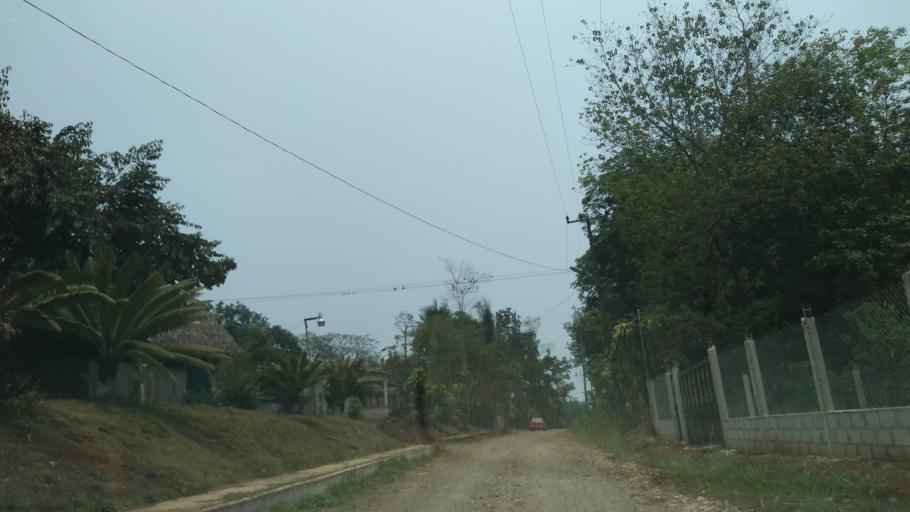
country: MX
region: Puebla
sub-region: San Sebastian Tlacotepec
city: San Martin Mazateopan
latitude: 18.4963
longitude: -96.7762
